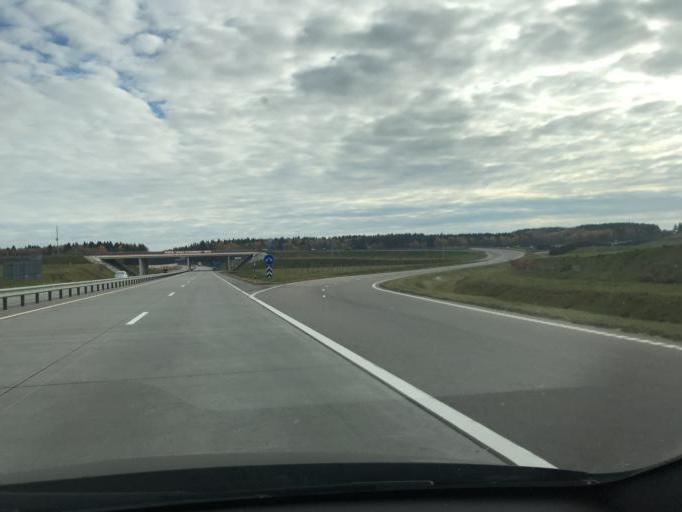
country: BY
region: Minsk
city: Zaslawye
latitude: 54.0686
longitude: 27.2879
